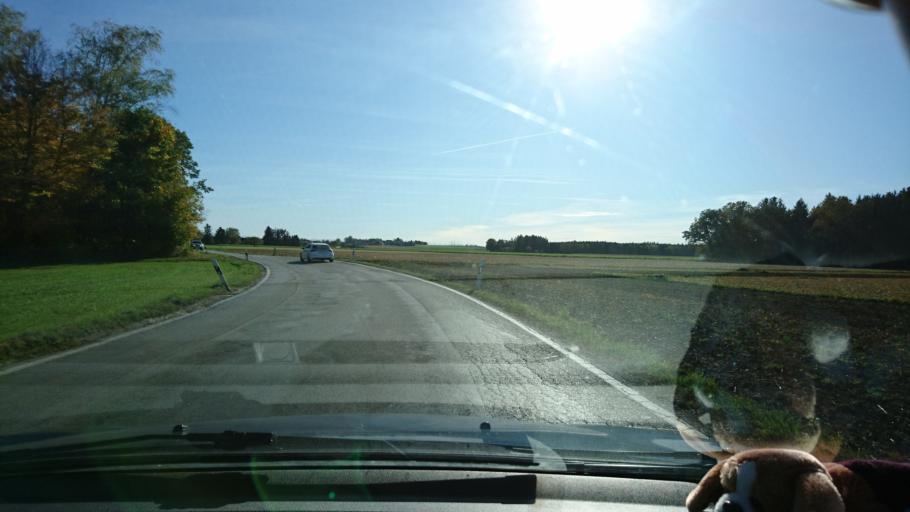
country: DE
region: Bavaria
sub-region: Upper Bavaria
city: Zorneding
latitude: 48.1197
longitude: 11.8330
